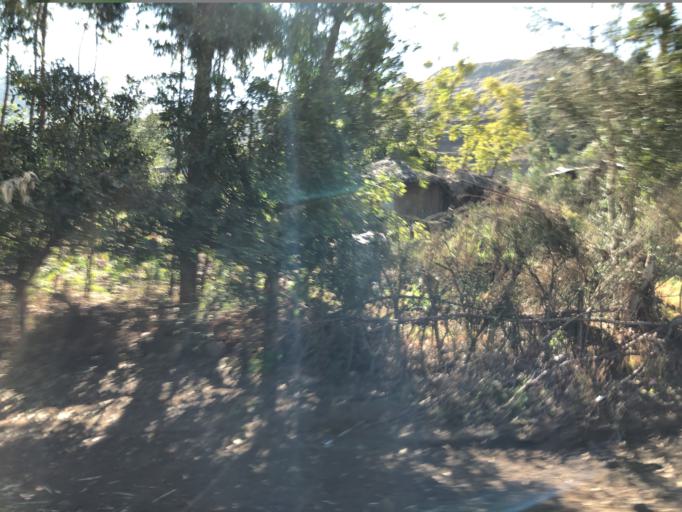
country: ET
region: Amhara
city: Lalibela
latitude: 12.0118
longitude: 39.0529
